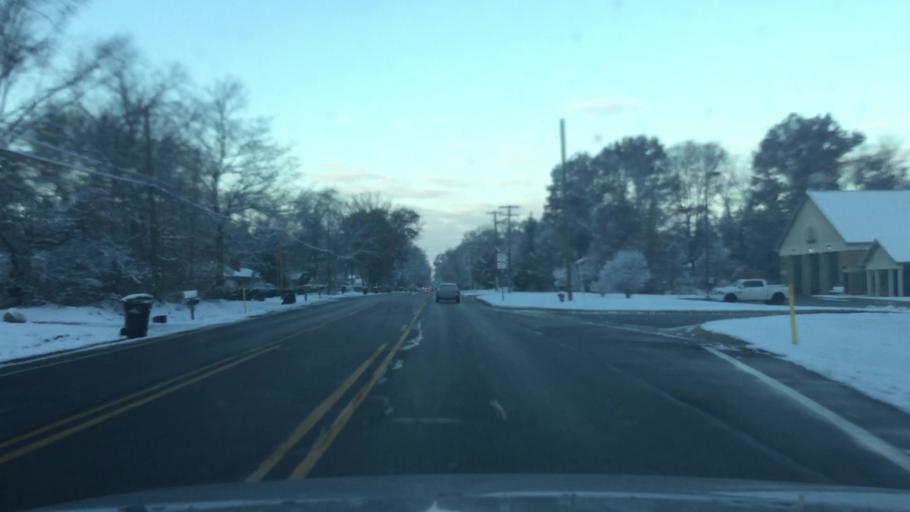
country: US
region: Michigan
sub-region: Oakland County
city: Wolverine Lake
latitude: 42.5918
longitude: -83.4639
